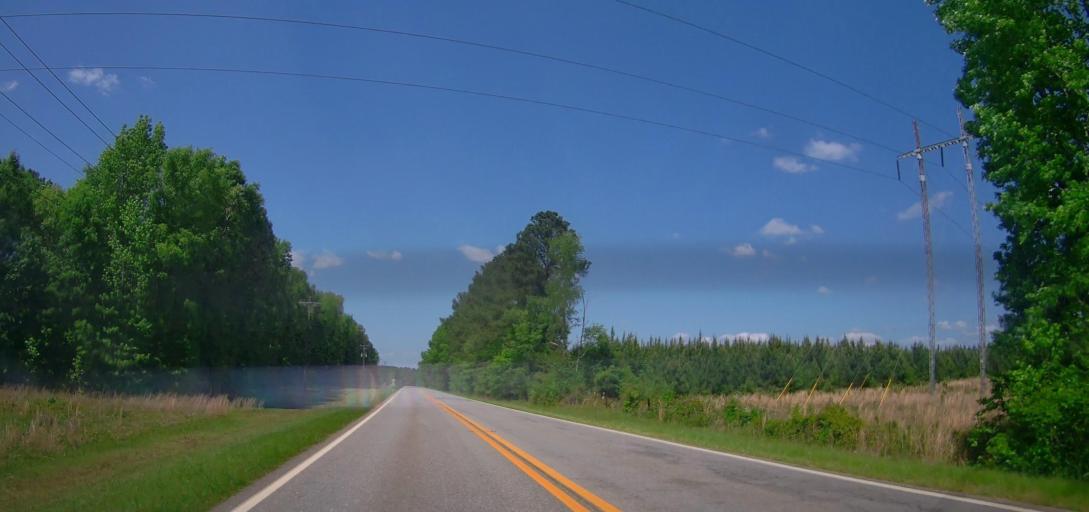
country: US
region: Georgia
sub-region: Putnam County
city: Eatonton
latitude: 33.3079
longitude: -83.3007
